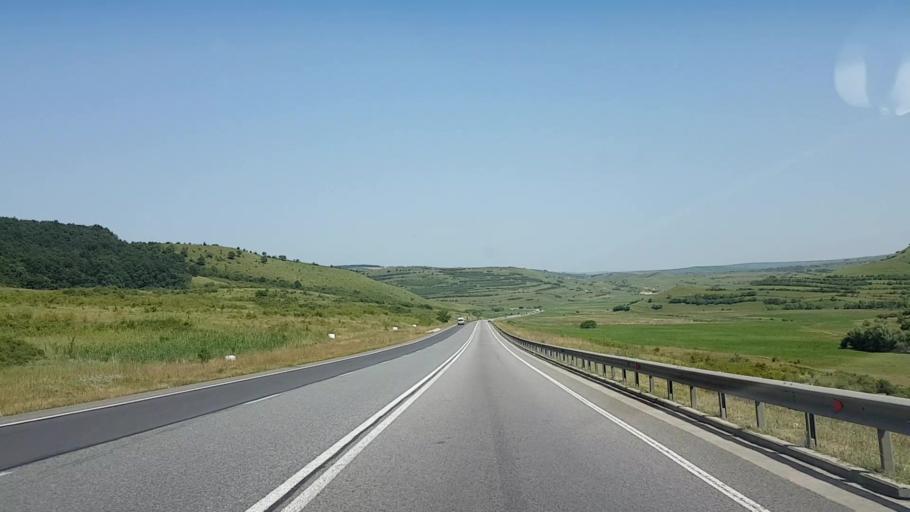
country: RO
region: Cluj
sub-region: Comuna Feleacu
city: Gheorghieni
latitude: 46.7324
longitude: 23.6839
